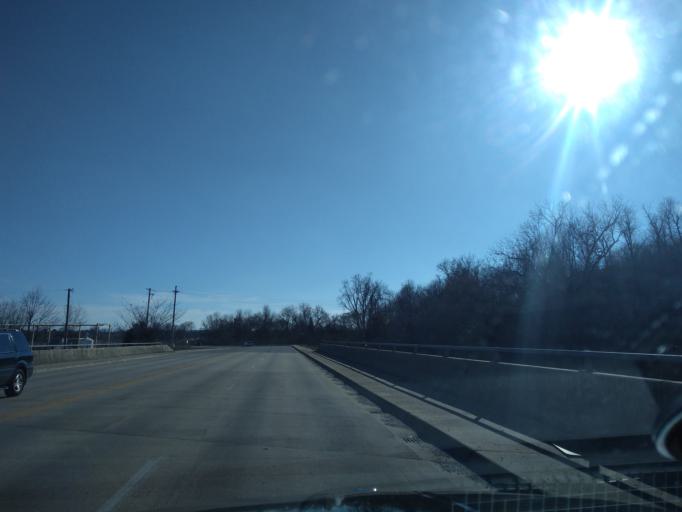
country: US
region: Arkansas
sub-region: Washington County
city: Johnson
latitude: 36.1232
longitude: -94.1627
